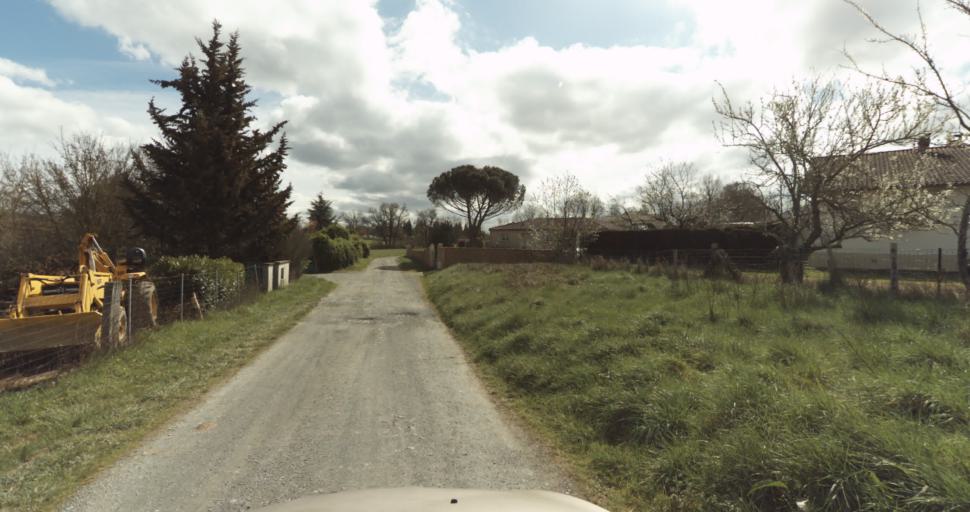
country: FR
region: Midi-Pyrenees
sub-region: Departement du Tarn
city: Puygouzon
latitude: 43.8908
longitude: 2.1531
